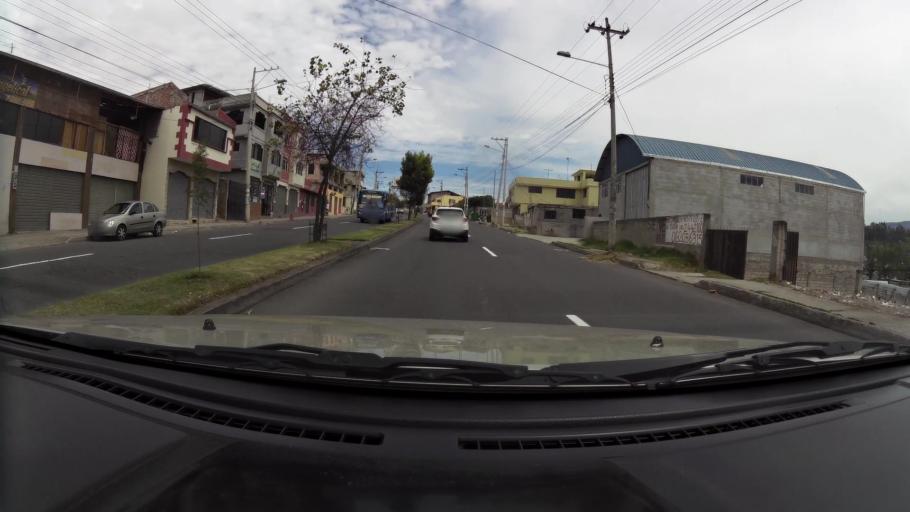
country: EC
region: Tungurahua
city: Pillaro
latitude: -1.1350
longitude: -78.5880
